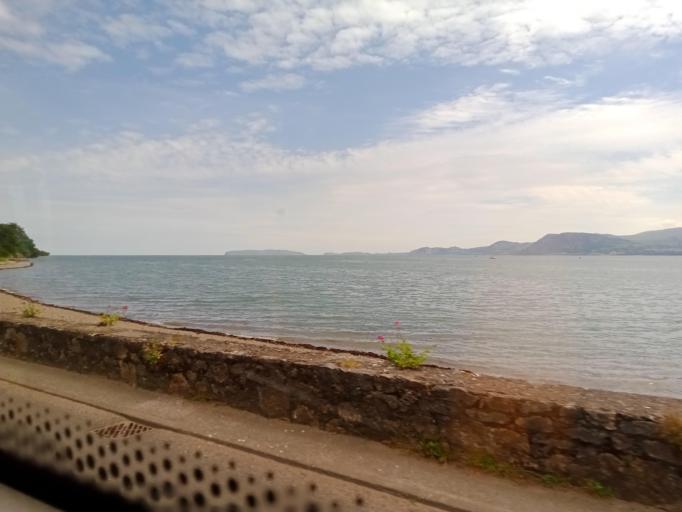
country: GB
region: Wales
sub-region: Anglesey
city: Llangoed
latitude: 53.2749
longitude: -4.0864
